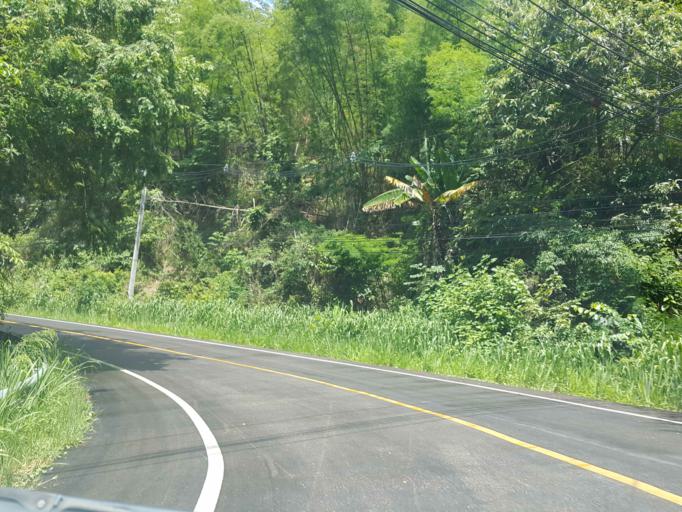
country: TH
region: Chiang Mai
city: Samoeng
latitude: 18.8539
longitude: 98.7733
